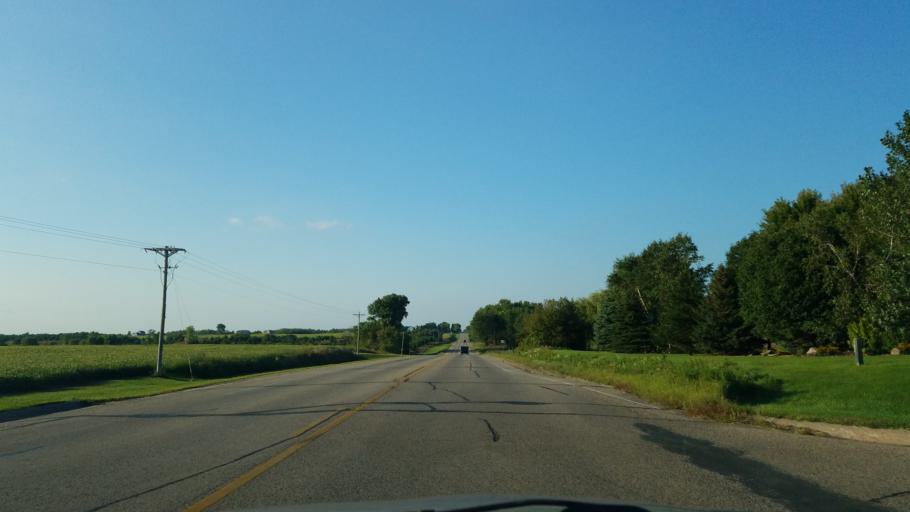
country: US
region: Wisconsin
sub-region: Saint Croix County
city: Roberts
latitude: 45.0501
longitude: -92.5373
